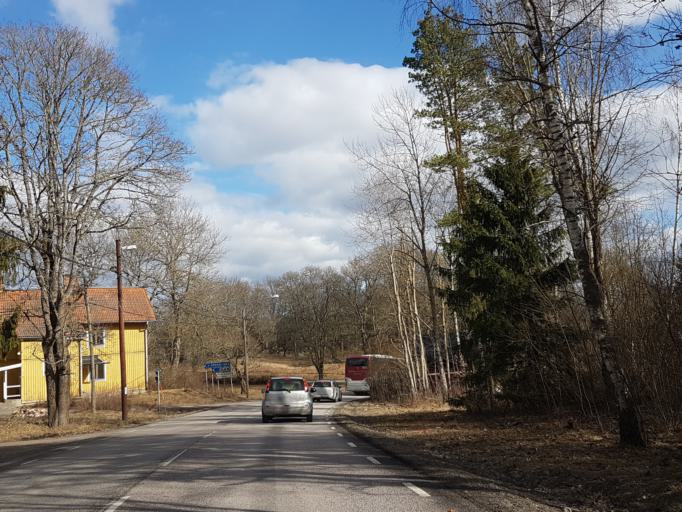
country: SE
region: Stockholm
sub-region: Norrtalje Kommun
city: Rimbo
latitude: 59.7376
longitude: 18.4885
